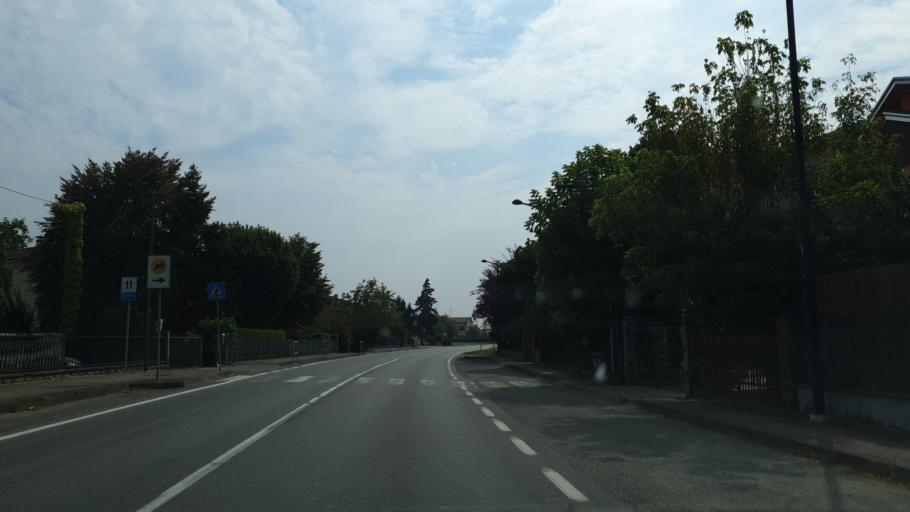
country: IT
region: Emilia-Romagna
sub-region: Provincia di Parma
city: San Secondo Parmense
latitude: 44.8971
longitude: 10.2573
